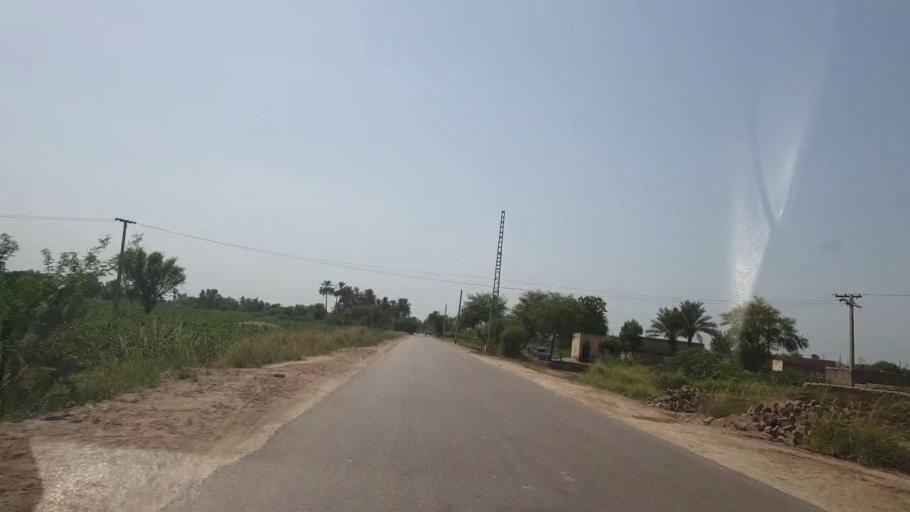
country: PK
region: Sindh
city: Bozdar
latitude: 27.1198
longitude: 68.5509
